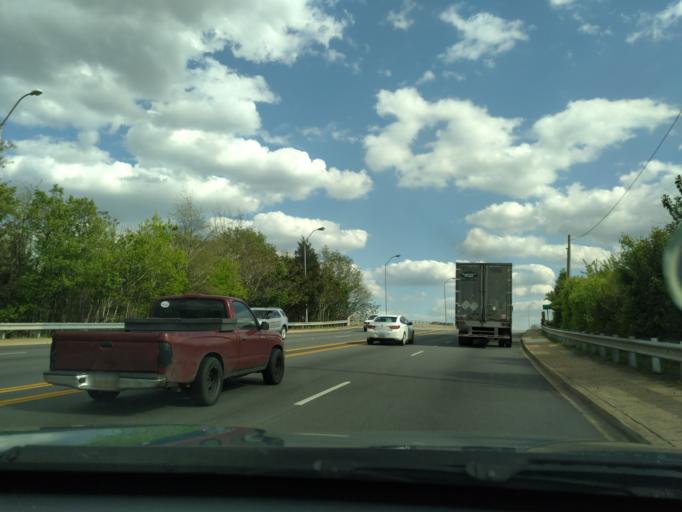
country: US
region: South Carolina
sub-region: Florence County
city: Florence
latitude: 34.2004
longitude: -79.7632
